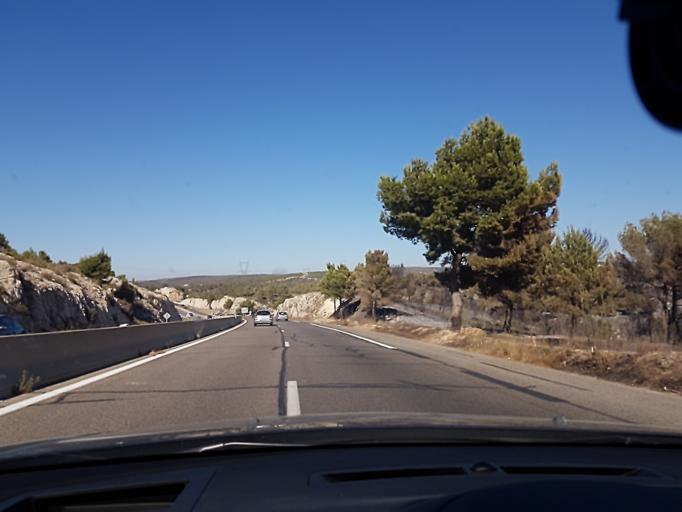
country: FR
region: Provence-Alpes-Cote d'Azur
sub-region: Departement des Bouches-du-Rhone
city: Ensues-la-Redonne
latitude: 43.3537
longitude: 5.1744
